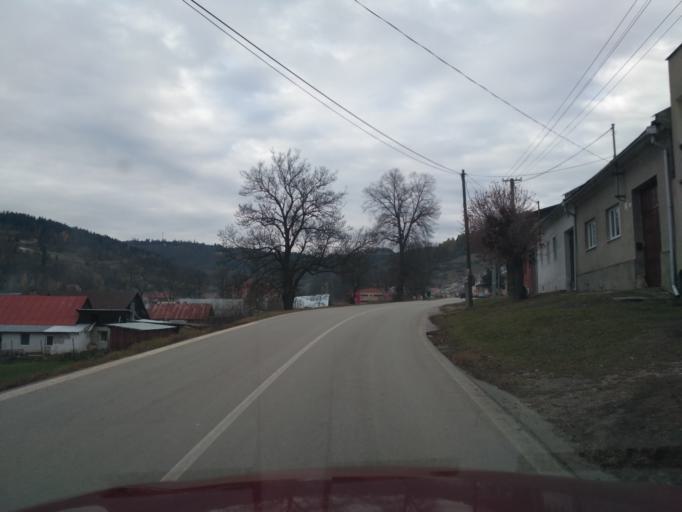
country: SK
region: Kosicky
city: Spisska Nova Ves
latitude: 48.8390
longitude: 20.6228
